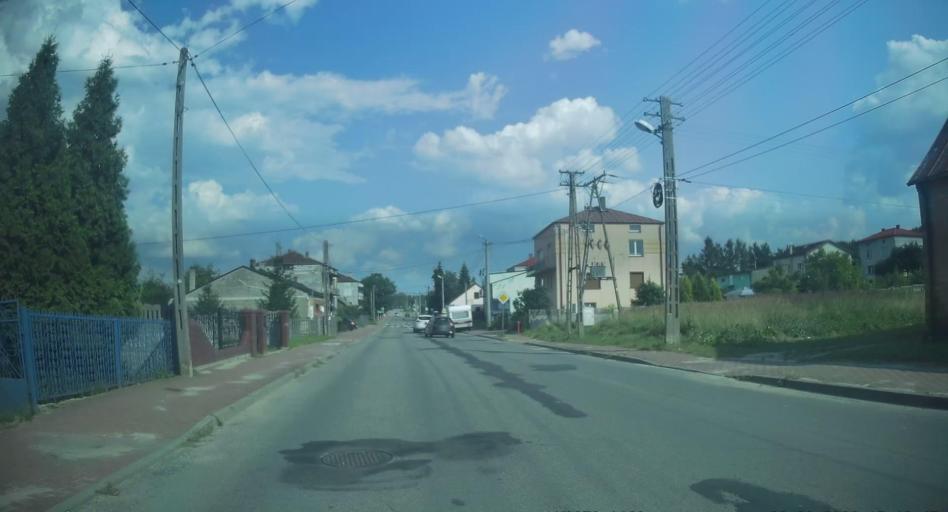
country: PL
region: Swietokrzyskie
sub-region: Powiat konecki
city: Radoszyce
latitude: 51.0728
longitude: 20.2632
